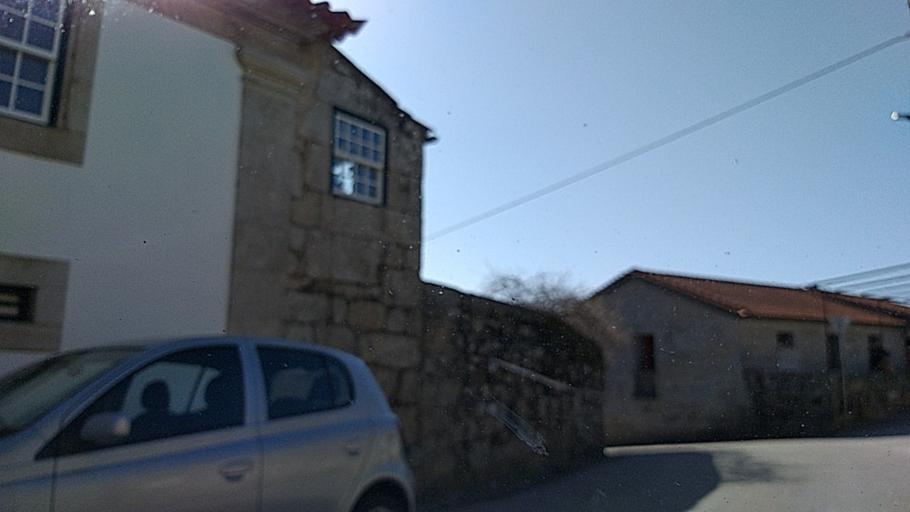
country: PT
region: Guarda
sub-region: Celorico da Beira
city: Celorico da Beira
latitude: 40.6745
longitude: -7.3978
